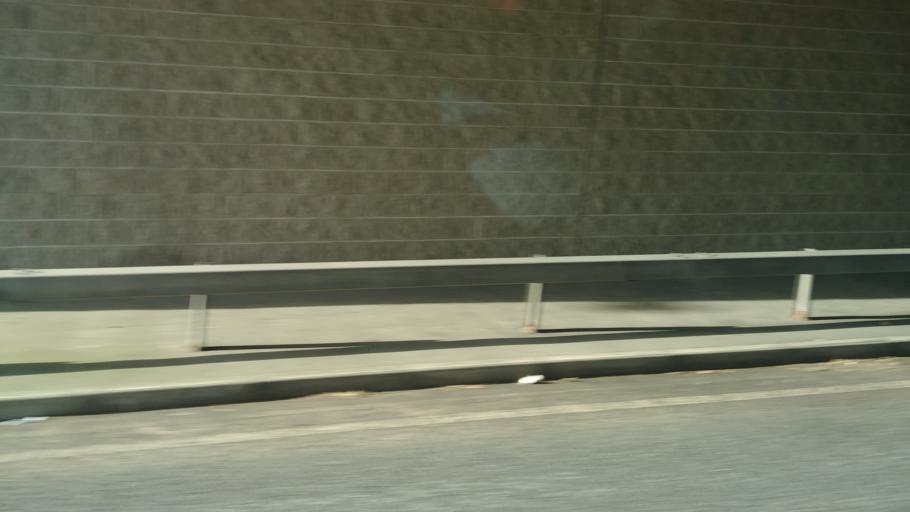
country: GB
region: Northern Ireland
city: Hillsborough
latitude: 54.4921
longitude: -6.0743
